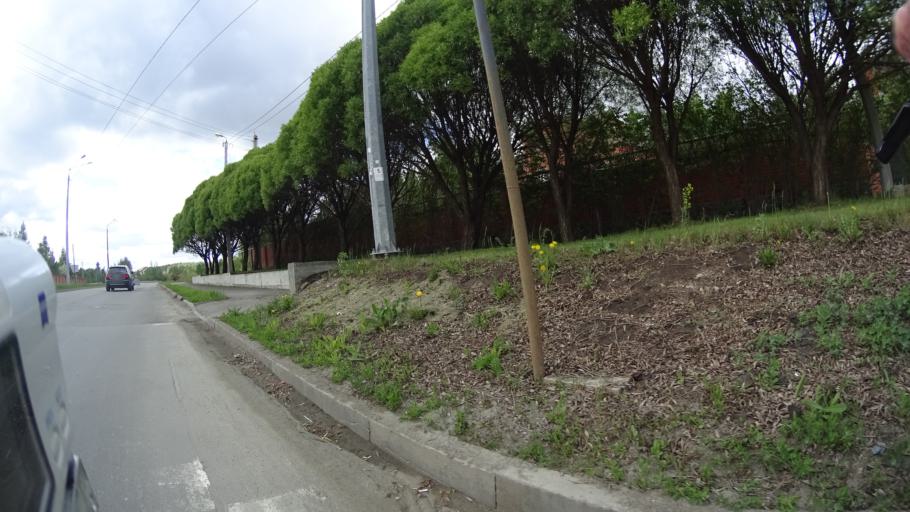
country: RU
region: Chelyabinsk
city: Sargazy
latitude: 55.1527
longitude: 61.2691
